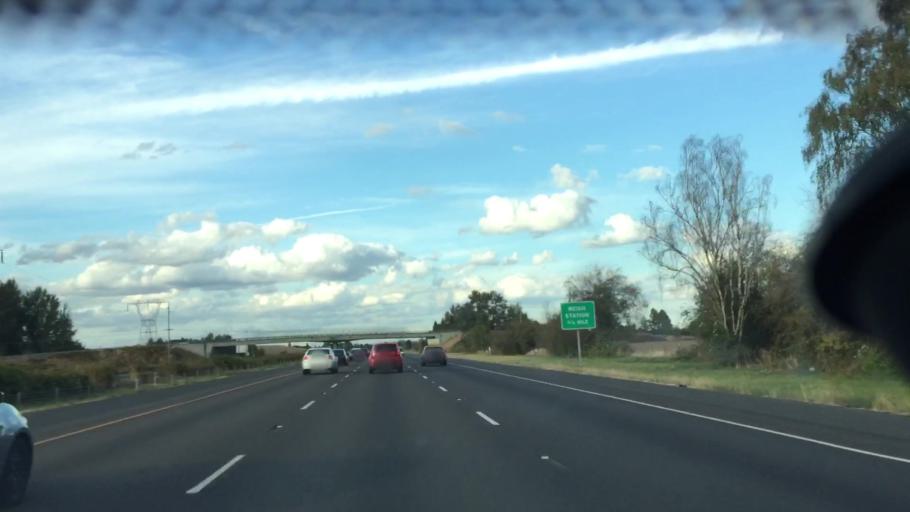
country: US
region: Oregon
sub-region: Marion County
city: Woodburn
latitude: 45.1647
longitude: -122.8665
